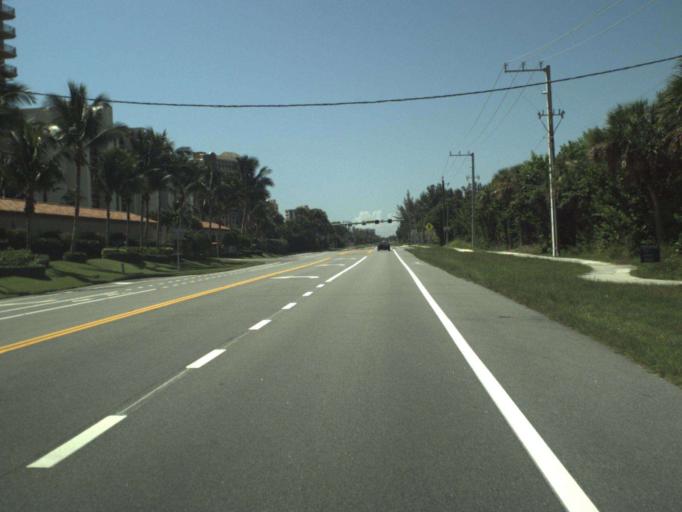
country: US
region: Florida
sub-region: Saint Lucie County
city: Fort Pierce North
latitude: 27.5139
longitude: -80.3080
